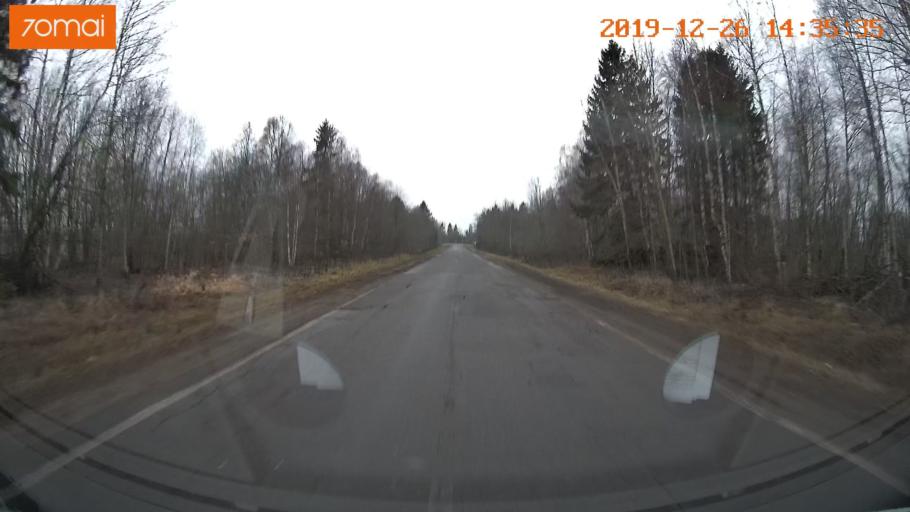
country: RU
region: Jaroslavl
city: Poshekhon'ye
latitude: 58.4190
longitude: 38.9826
